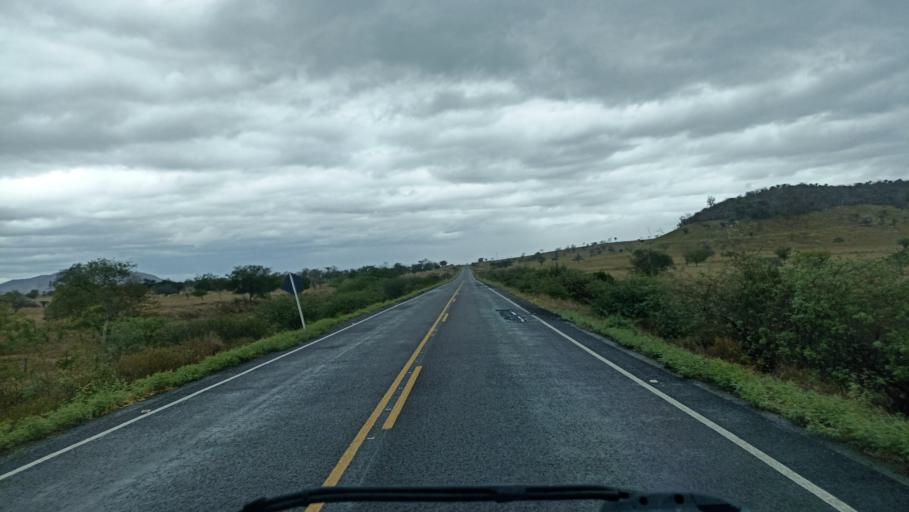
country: BR
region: Bahia
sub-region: Iacu
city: Iacu
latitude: -12.9635
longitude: -40.4844
